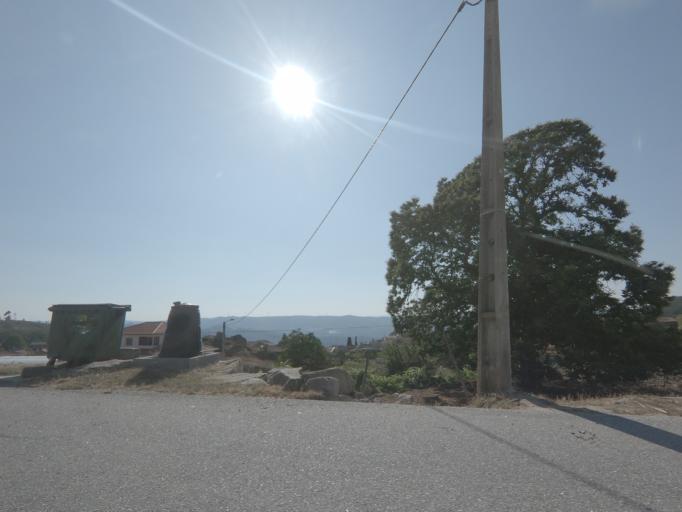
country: PT
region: Viseu
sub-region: Tabuaco
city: Tabuaco
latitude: 41.0490
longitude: -7.5676
